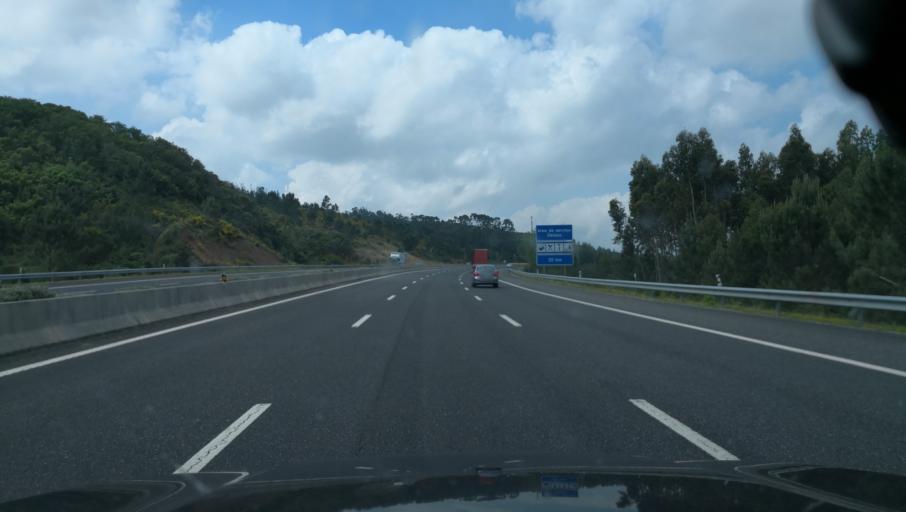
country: PT
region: Leiria
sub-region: Nazare
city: Nazare
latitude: 39.5414
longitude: -9.0636
